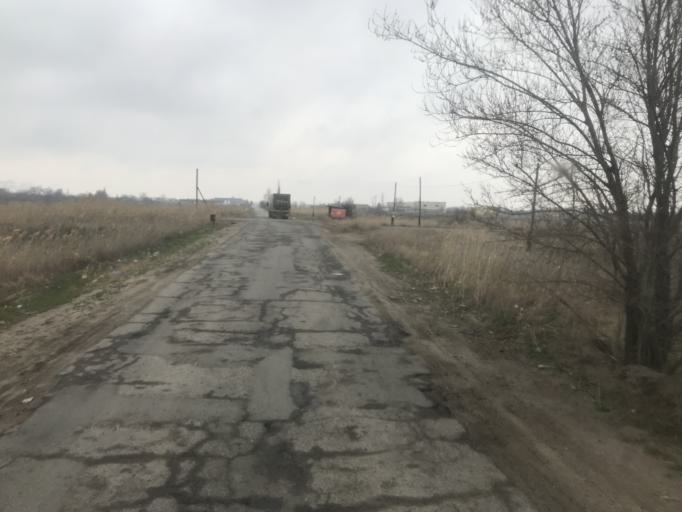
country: RU
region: Volgograd
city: Svetlyy Yar
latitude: 48.5185
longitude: 44.6270
